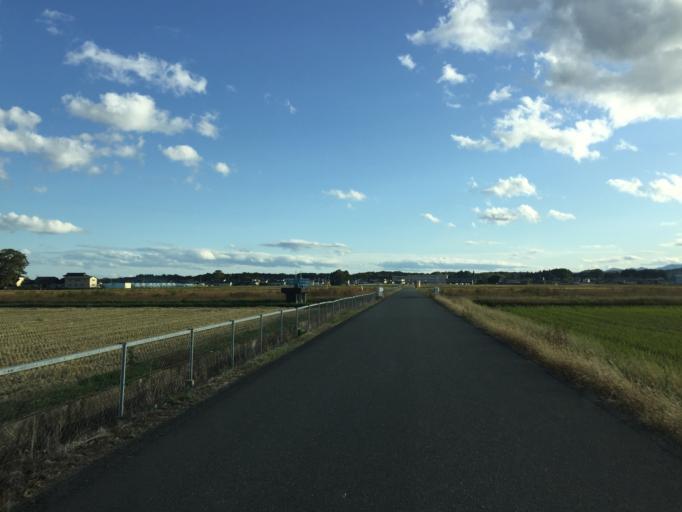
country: JP
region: Miyagi
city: Marumori
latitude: 37.7964
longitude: 140.9489
